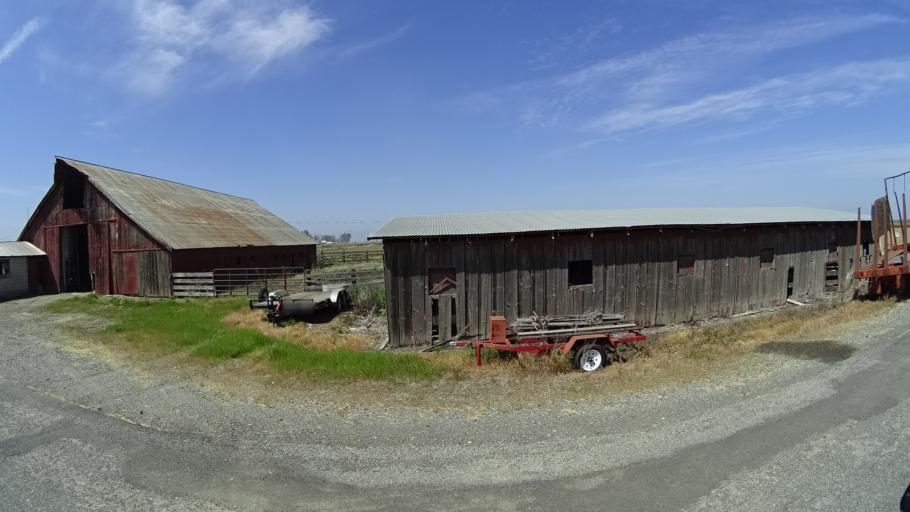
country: US
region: California
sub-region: Glenn County
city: Hamilton City
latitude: 39.5981
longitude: -122.0463
